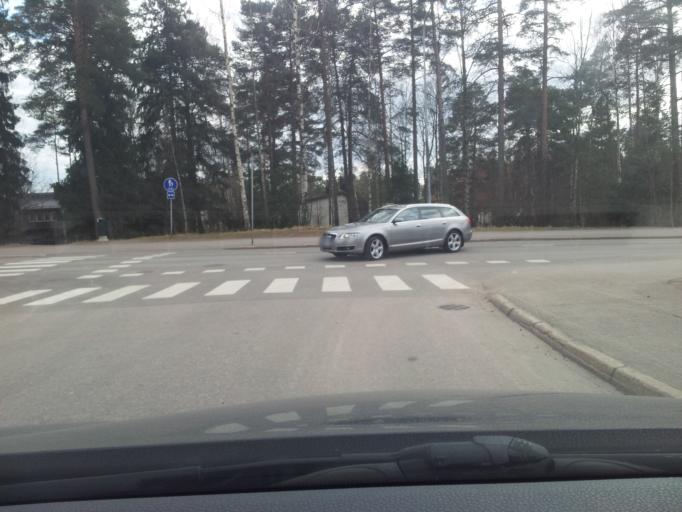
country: FI
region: Uusimaa
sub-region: Helsinki
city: Koukkuniemi
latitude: 60.1728
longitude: 24.7422
